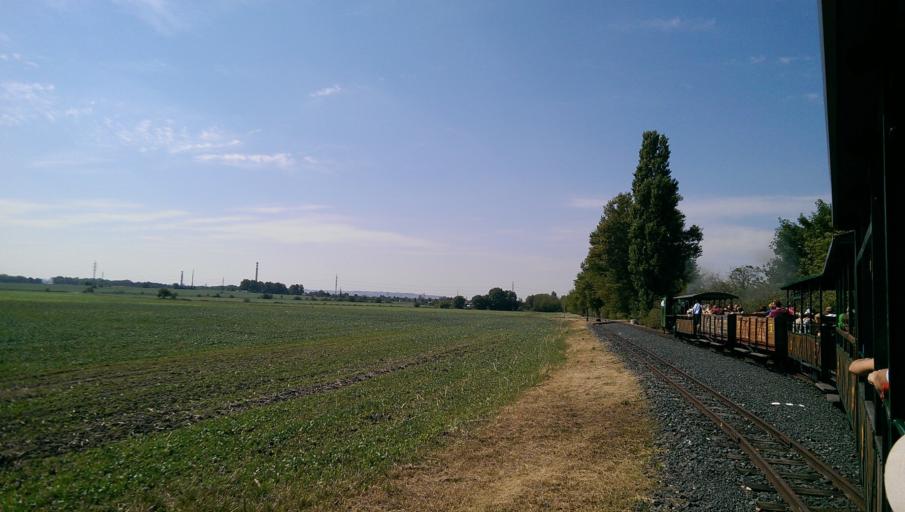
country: CZ
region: Central Bohemia
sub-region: Okres Kolin
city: Kolin
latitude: 50.0537
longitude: 15.2319
